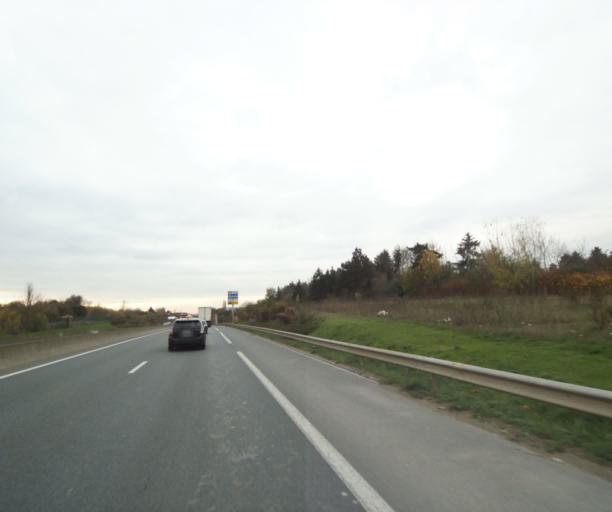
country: FR
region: Ile-de-France
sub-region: Departement du Val-d'Oise
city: Le Thillay
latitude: 48.9860
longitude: 2.4715
